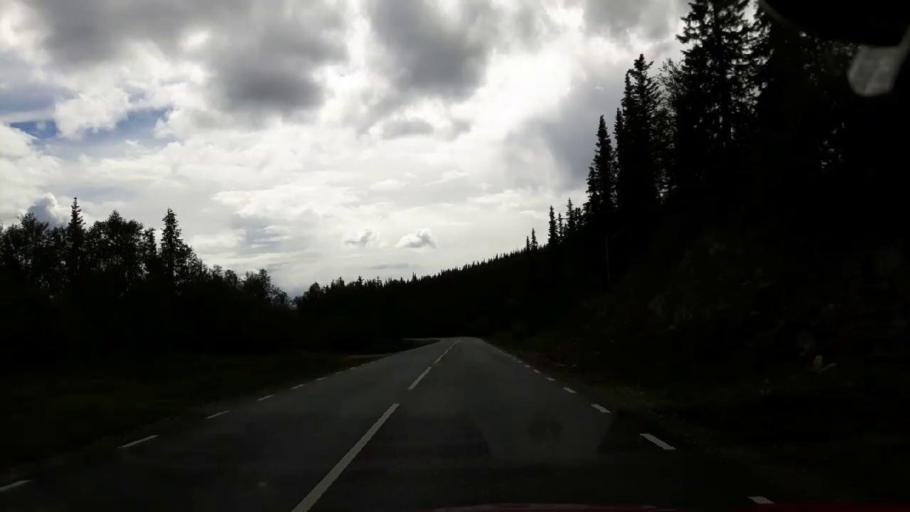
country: NO
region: Nord-Trondelag
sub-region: Royrvik
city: Royrvik
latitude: 64.8161
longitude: 14.0624
